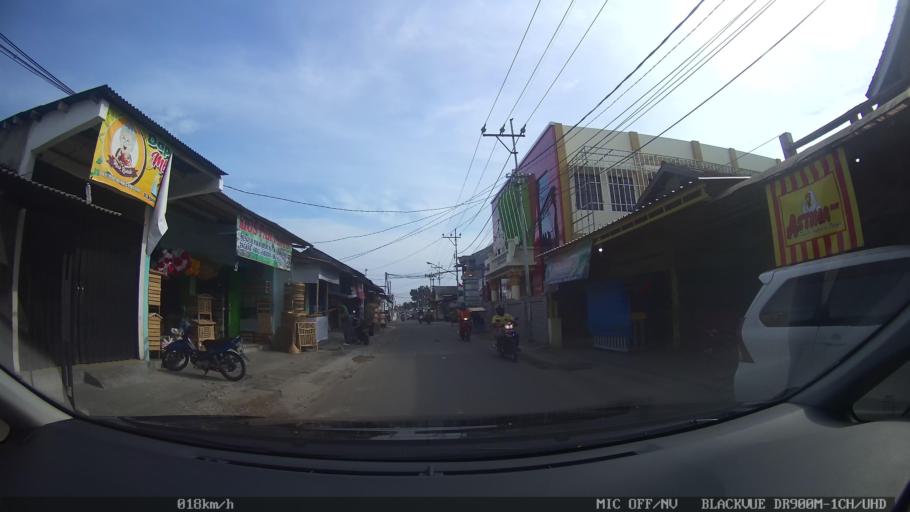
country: ID
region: Lampung
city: Bandarlampung
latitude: -5.4078
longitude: 105.2634
